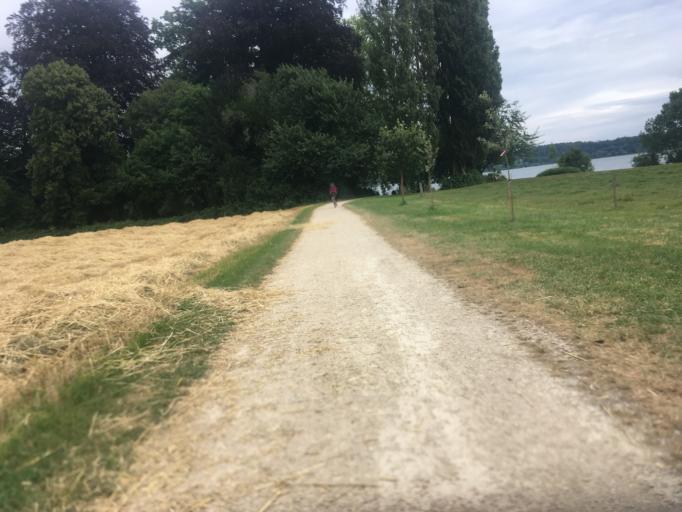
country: CH
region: Bern
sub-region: Jura bernois
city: La Neuveville
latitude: 47.0697
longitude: 7.1440
